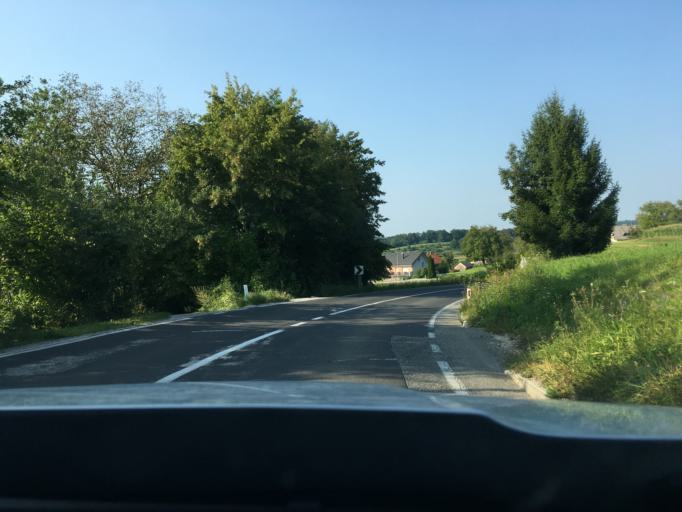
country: SI
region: Novo Mesto
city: Novo Mesto
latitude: 45.7652
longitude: 15.1964
